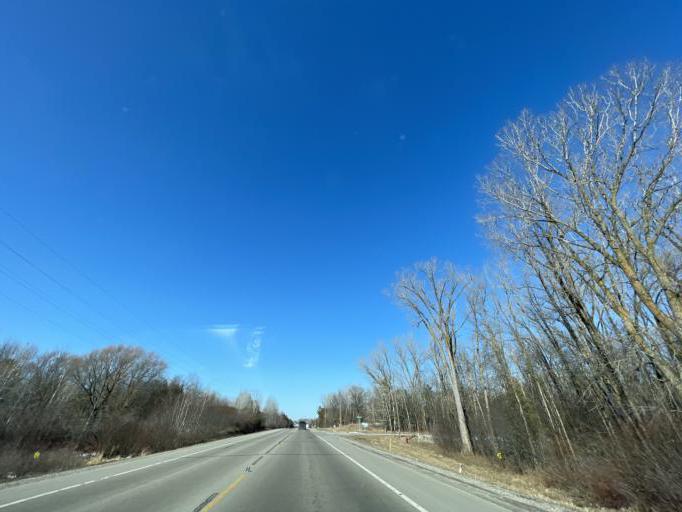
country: US
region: Wisconsin
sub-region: Brown County
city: Howard
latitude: 44.5955
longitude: -88.0779
